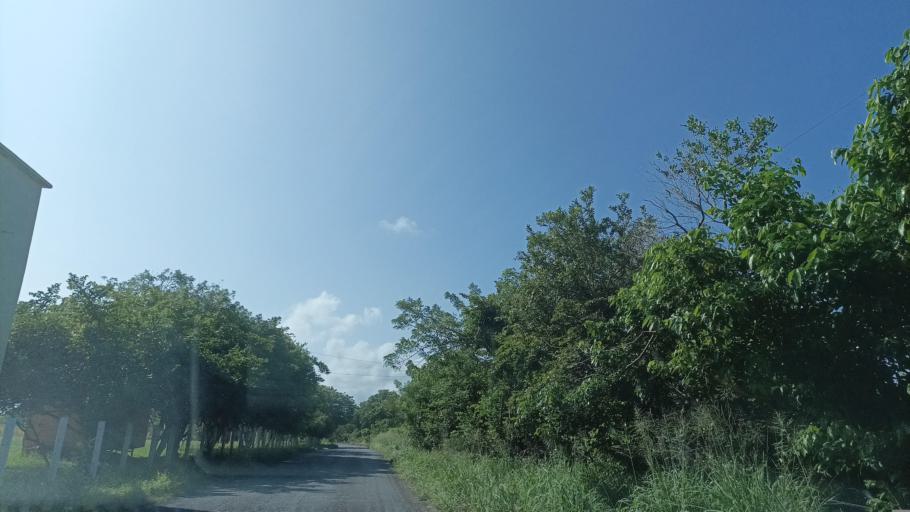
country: MX
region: Veracruz
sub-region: Pajapan
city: Pajapan
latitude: 18.2333
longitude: -94.6197
